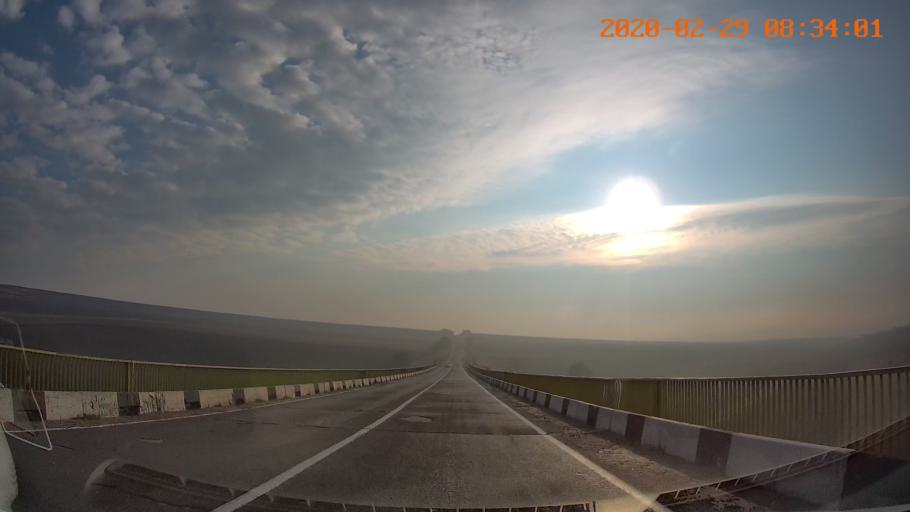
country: MD
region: Anenii Noi
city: Anenii Noi
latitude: 46.9260
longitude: 29.3016
